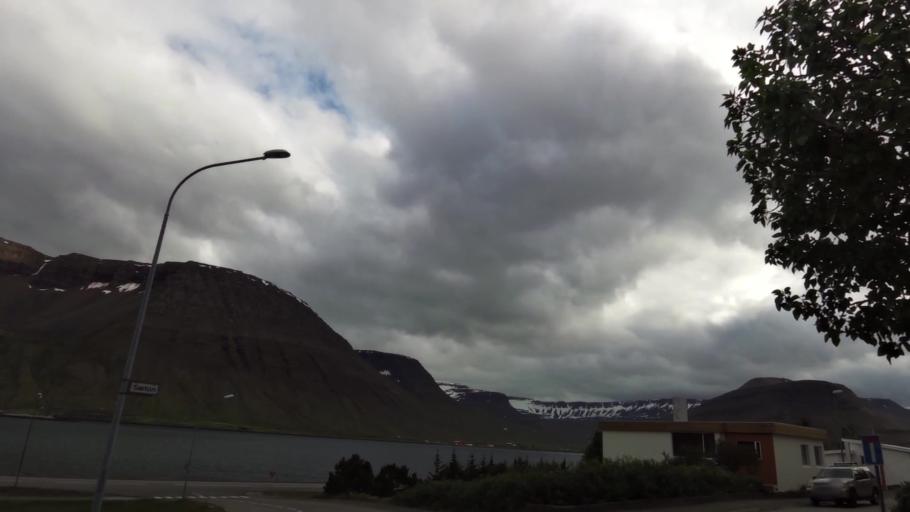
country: IS
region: Westfjords
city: Isafjoerdur
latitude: 66.0717
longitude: -23.1406
